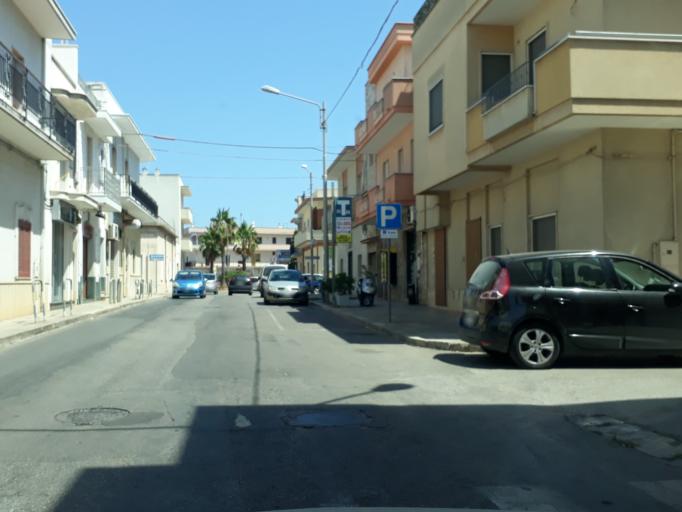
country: IT
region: Apulia
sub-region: Provincia di Brindisi
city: Carovigno
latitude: 40.7032
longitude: 17.6627
